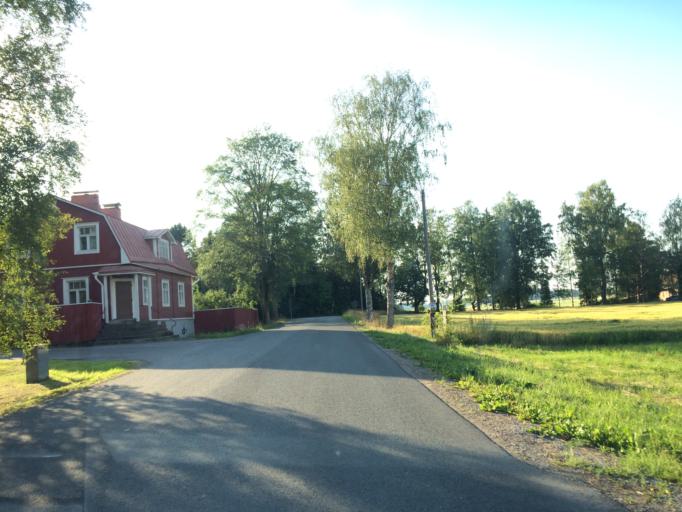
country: FI
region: Haeme
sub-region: Haemeenlinna
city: Parola
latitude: 61.0379
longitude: 24.4015
